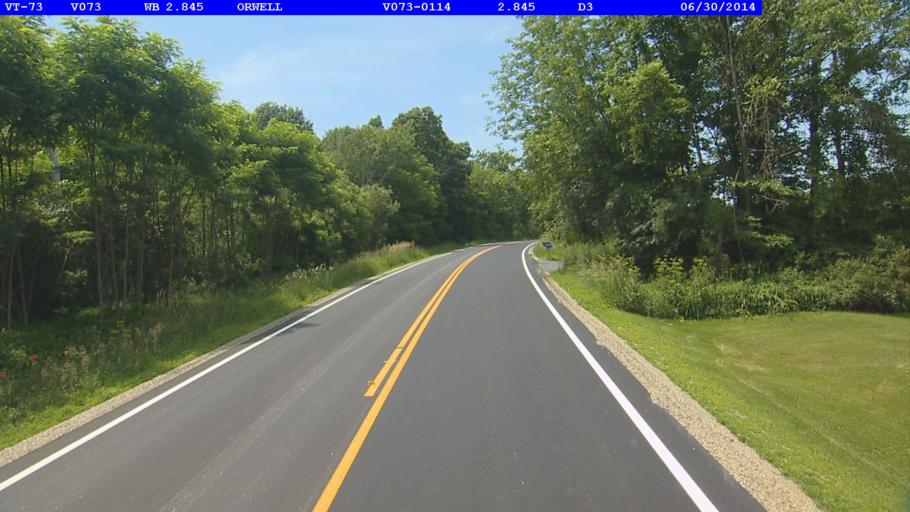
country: US
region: Vermont
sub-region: Rutland County
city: Brandon
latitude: 43.8014
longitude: -73.2504
